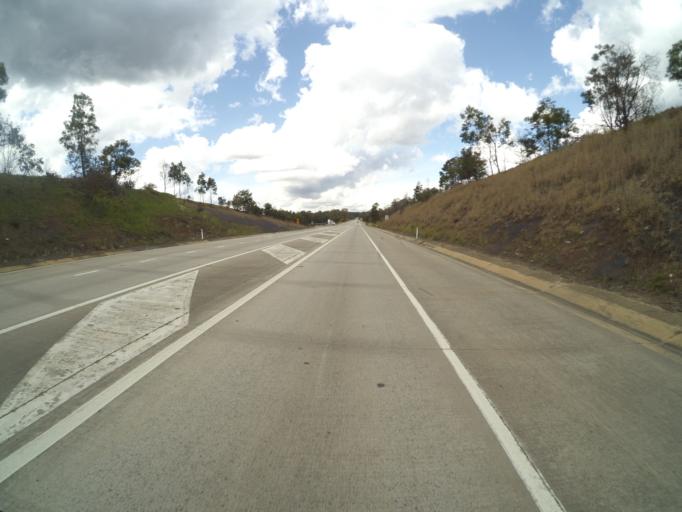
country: AU
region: New South Wales
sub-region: Wollondilly
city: Douglas Park
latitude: -34.2410
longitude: 150.6940
